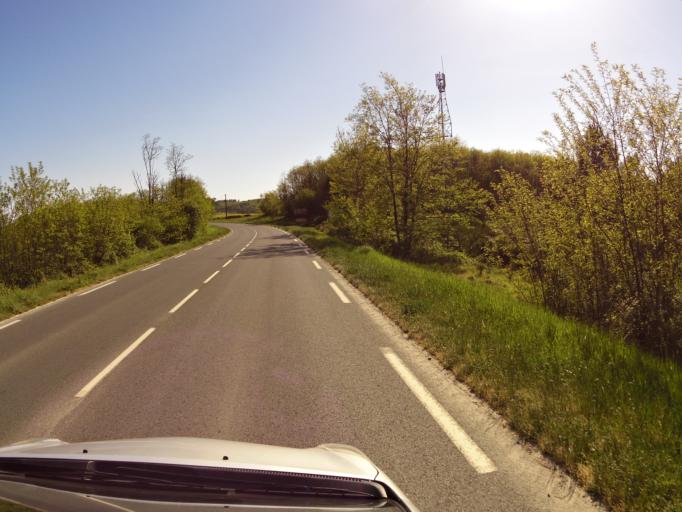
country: FR
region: Aquitaine
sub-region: Departement de la Dordogne
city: Sarlat-la-Caneda
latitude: 44.9538
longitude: 1.2252
